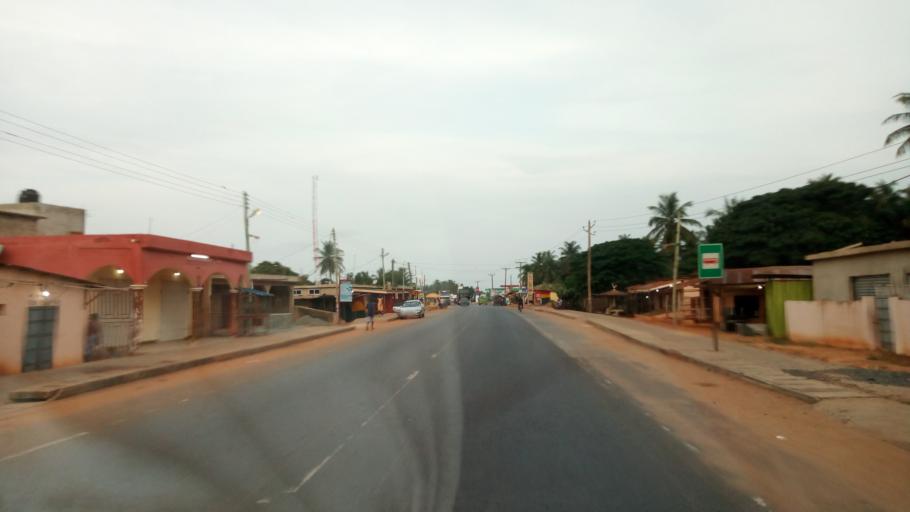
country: TG
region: Maritime
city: Lome
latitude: 6.1135
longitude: 1.1654
